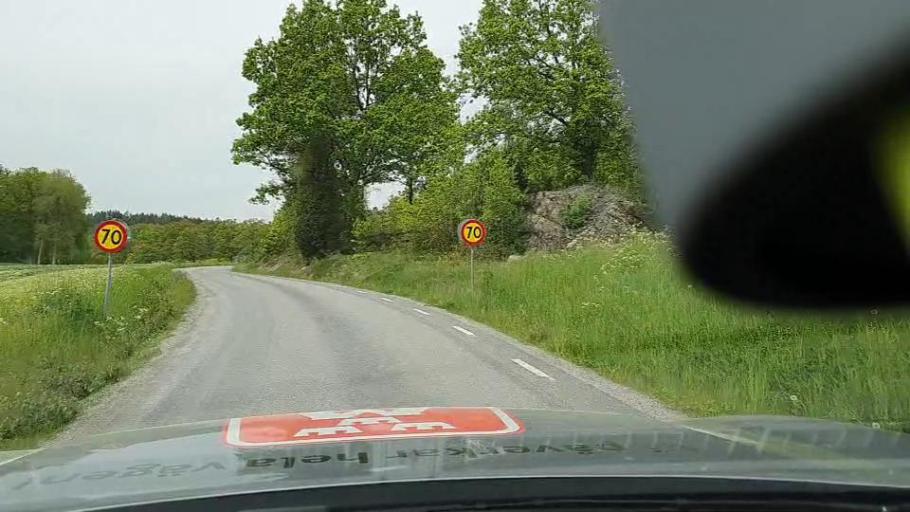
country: SE
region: Soedermanland
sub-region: Flens Kommun
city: Halleforsnas
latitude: 59.1017
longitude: 16.4780
